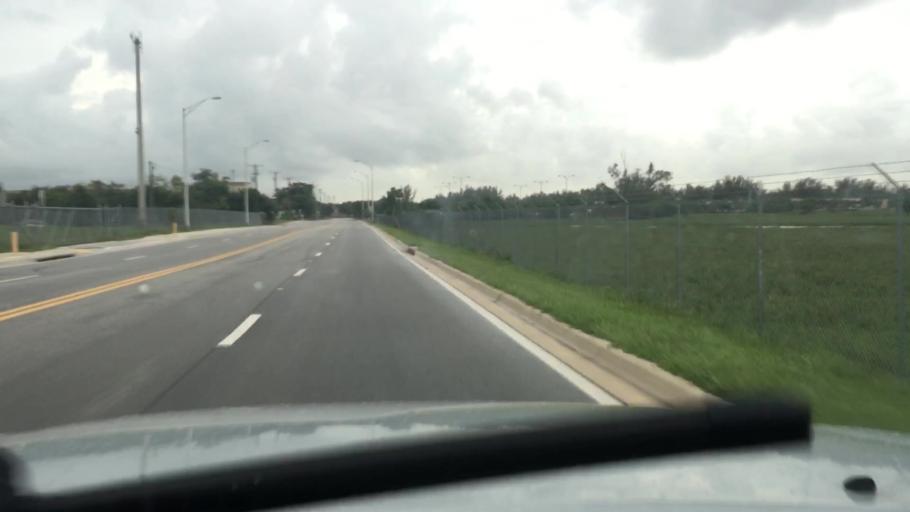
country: US
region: Florida
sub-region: Miami-Dade County
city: Doral
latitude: 25.8022
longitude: -80.3453
